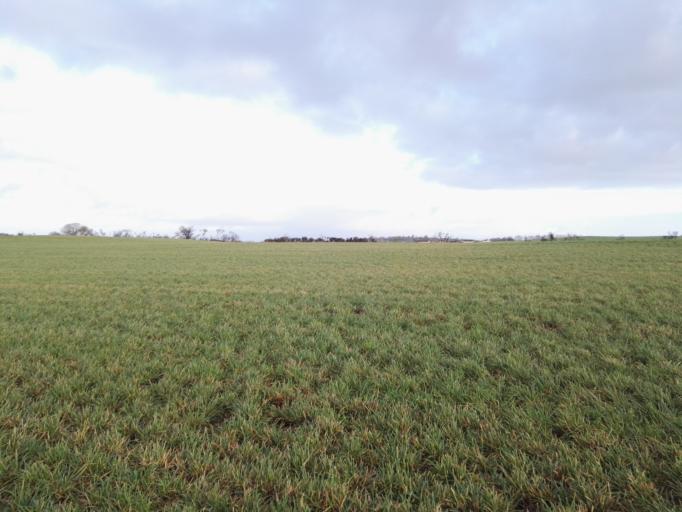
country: DK
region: Capital Region
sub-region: Frederikssund Kommune
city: Jaegerspris
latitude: 55.8448
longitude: 11.9714
